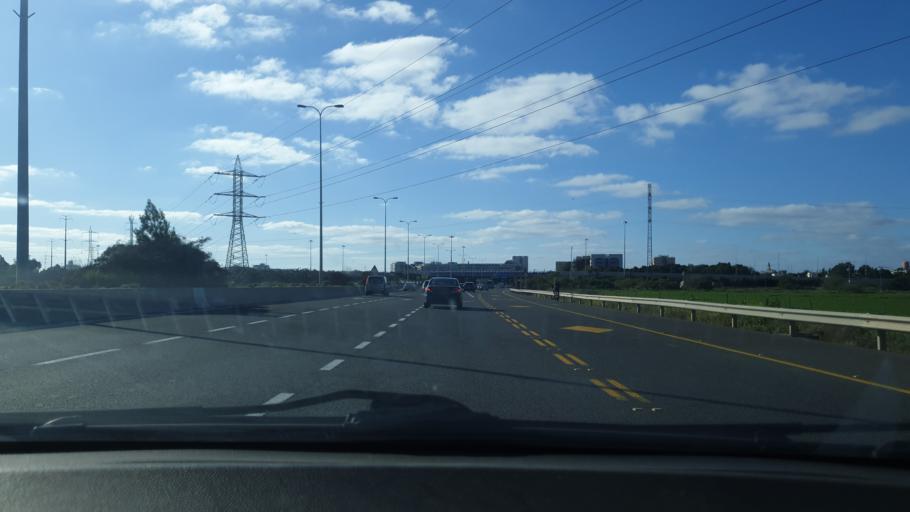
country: IL
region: Tel Aviv
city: Holon
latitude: 32.0365
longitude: 34.7826
